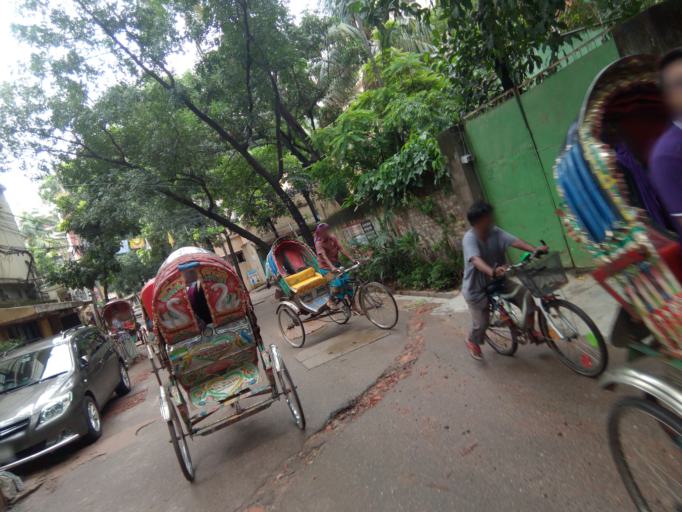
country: BD
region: Dhaka
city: Azimpur
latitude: 23.7547
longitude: 90.3687
